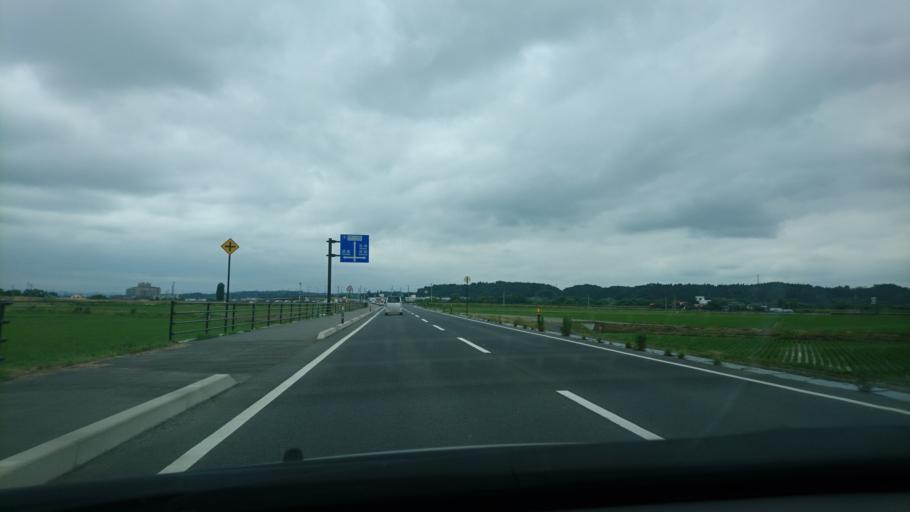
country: JP
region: Miyagi
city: Furukawa
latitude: 38.7470
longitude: 141.0315
